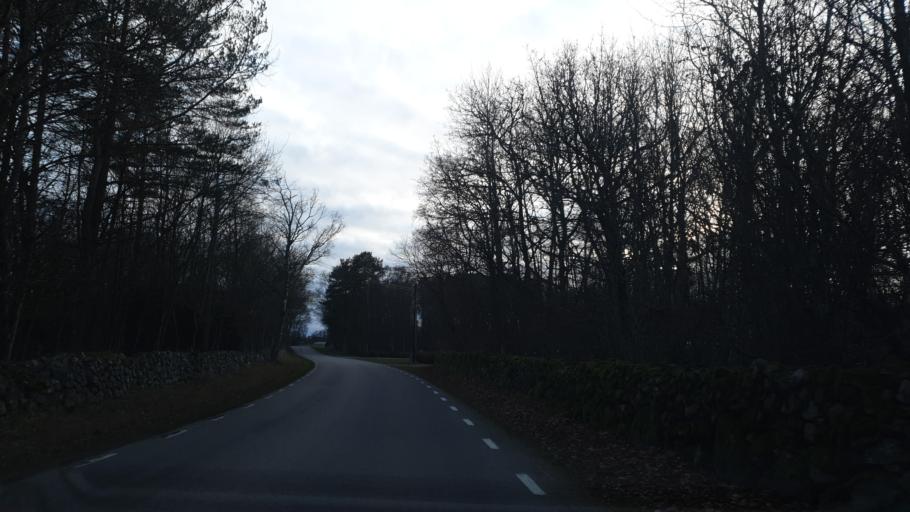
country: SE
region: Blekinge
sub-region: Karlskrona Kommun
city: Jaemjoe
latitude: 56.1976
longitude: 15.9496
